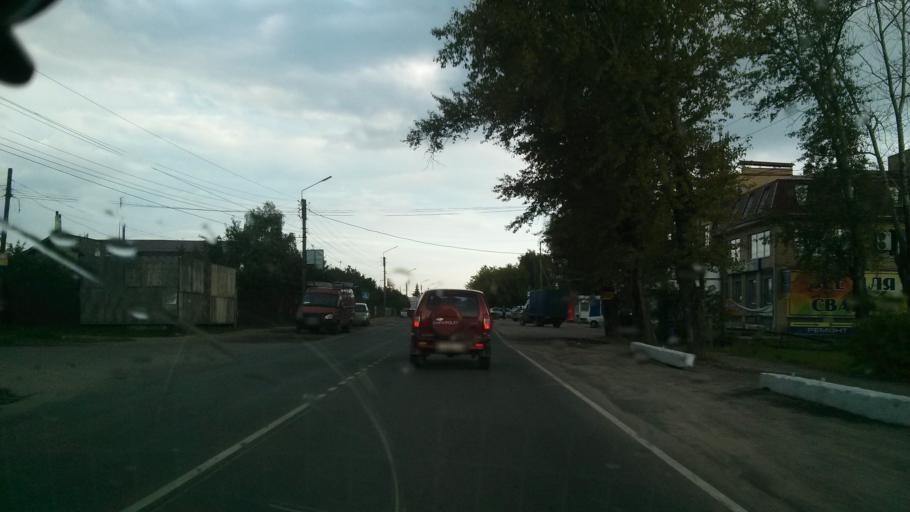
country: RU
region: Vladimir
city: Murom
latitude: 55.5934
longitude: 42.0344
